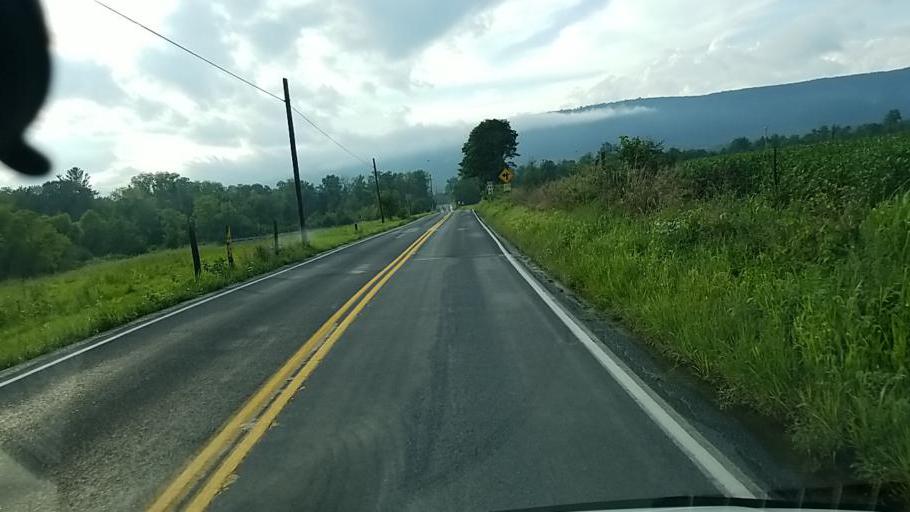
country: US
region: Pennsylvania
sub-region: Cumberland County
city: Newville
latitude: 40.1964
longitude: -77.4995
